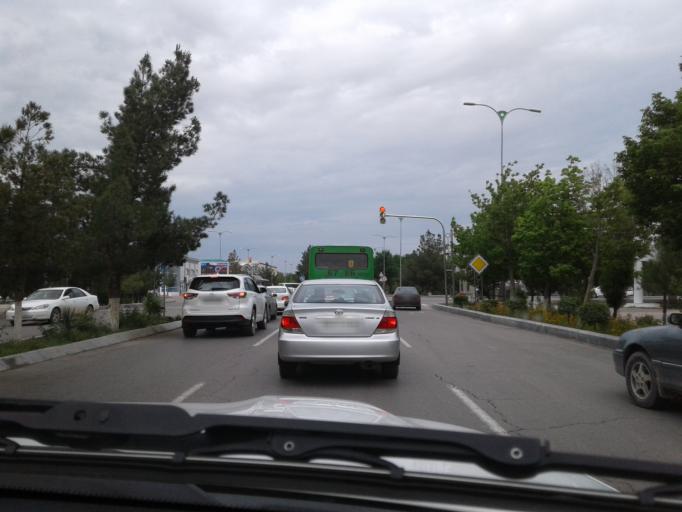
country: TM
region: Mary
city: Mary
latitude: 37.5904
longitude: 61.8691
